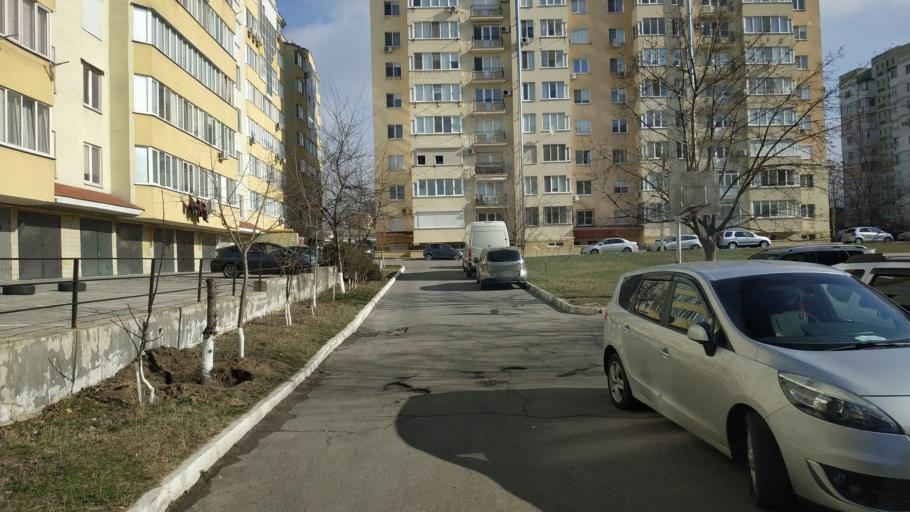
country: MD
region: Chisinau
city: Vatra
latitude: 47.0392
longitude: 28.7640
